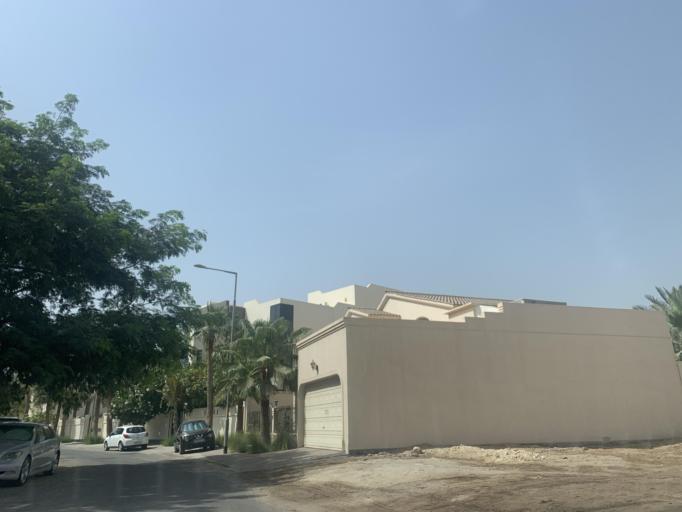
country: BH
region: Manama
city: Jidd Hafs
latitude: 26.2010
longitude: 50.5031
